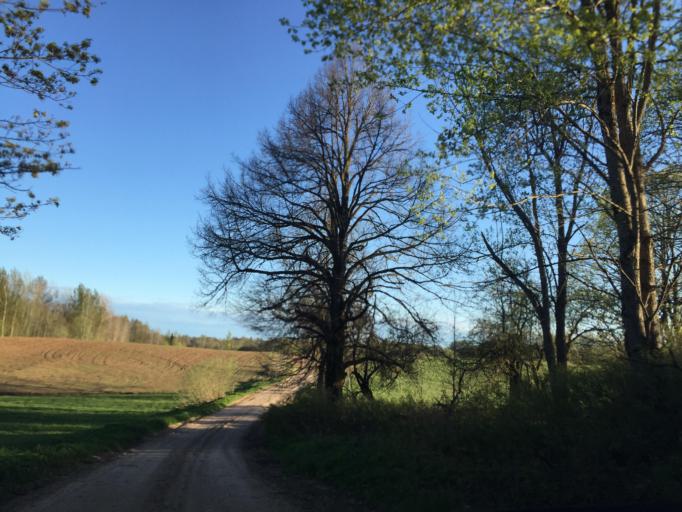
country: LV
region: Vecpiebalga
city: Vecpiebalga
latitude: 56.8448
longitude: 25.9571
